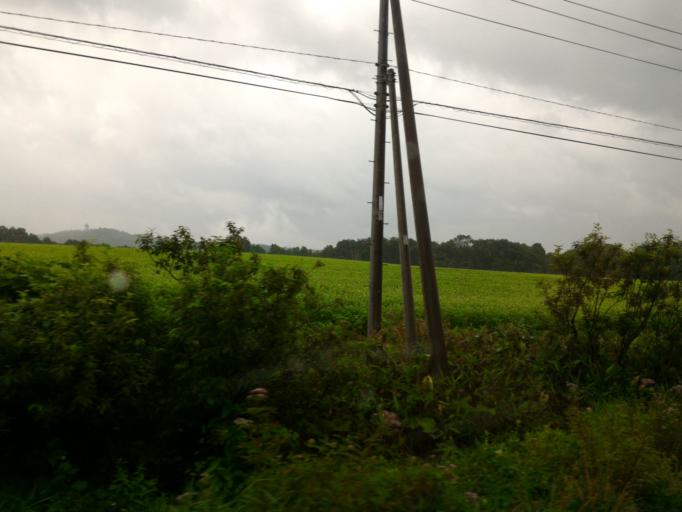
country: JP
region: Hokkaido
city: Nayoro
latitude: 44.6539
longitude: 142.2683
